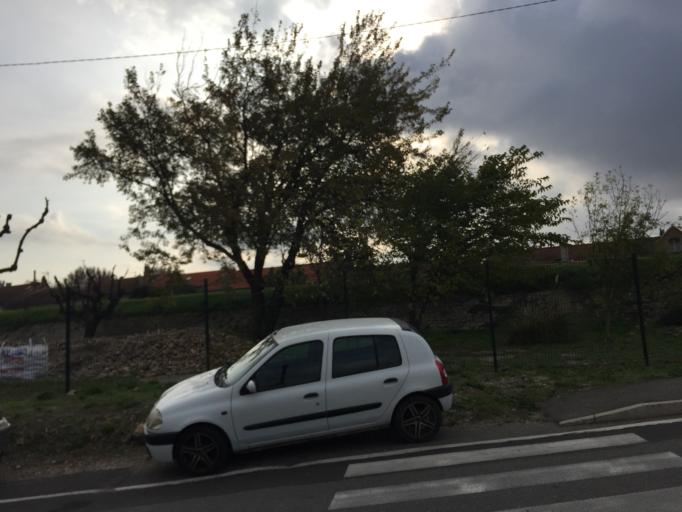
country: FR
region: Provence-Alpes-Cote d'Azur
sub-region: Departement du Vaucluse
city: Avignon
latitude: 43.9539
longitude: 4.8240
